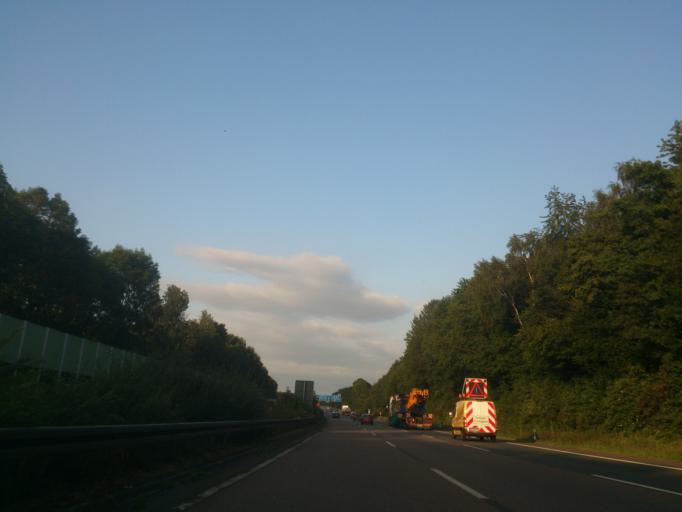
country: DE
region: North Rhine-Westphalia
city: Herdecke
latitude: 51.4417
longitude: 7.4635
